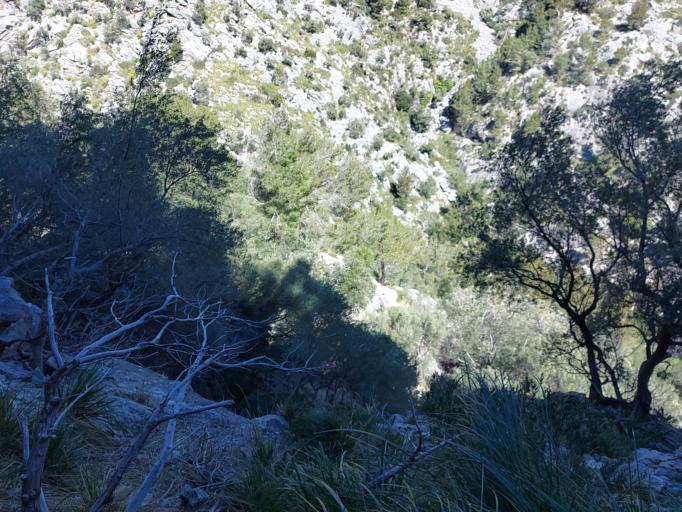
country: ES
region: Balearic Islands
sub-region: Illes Balears
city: Mancor de la Vall
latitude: 39.7682
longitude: 2.8098
